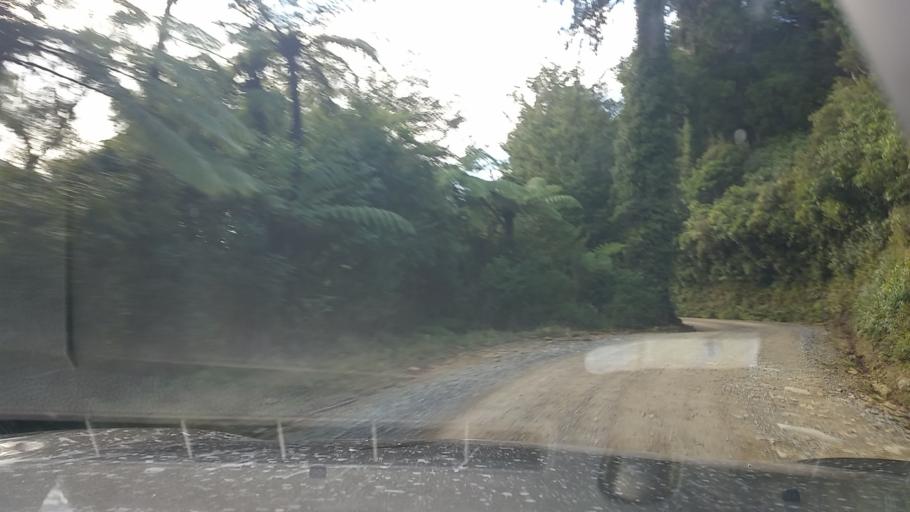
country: NZ
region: Marlborough
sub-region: Marlborough District
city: Picton
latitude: -41.1097
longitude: 174.1318
